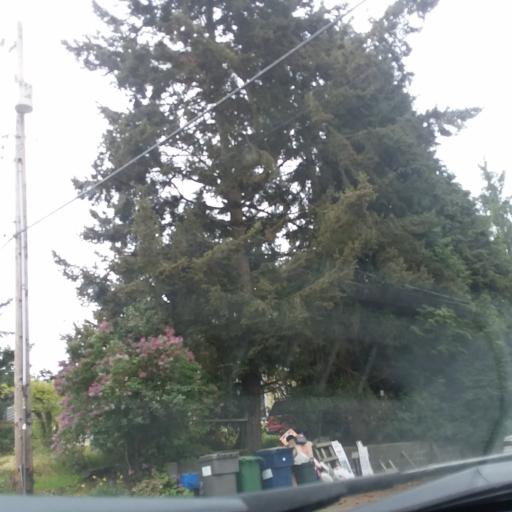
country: US
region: Washington
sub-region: King County
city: Boulevard Park
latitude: 47.5027
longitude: -122.3179
